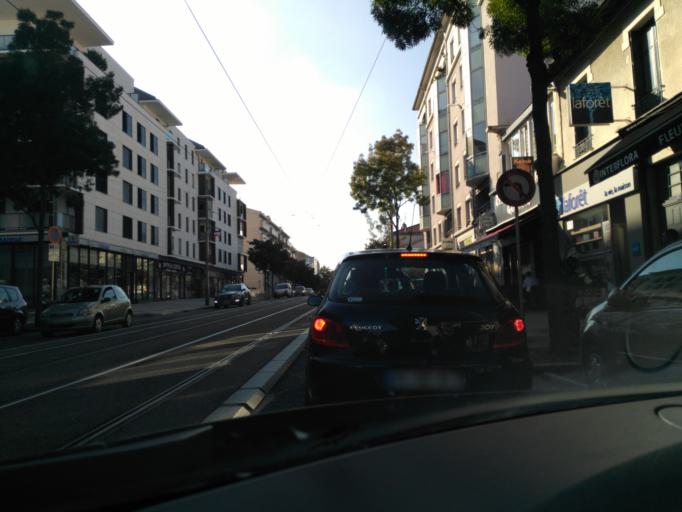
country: FR
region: Rhone-Alpes
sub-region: Departement du Rhone
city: Bron
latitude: 45.7328
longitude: 4.9110
